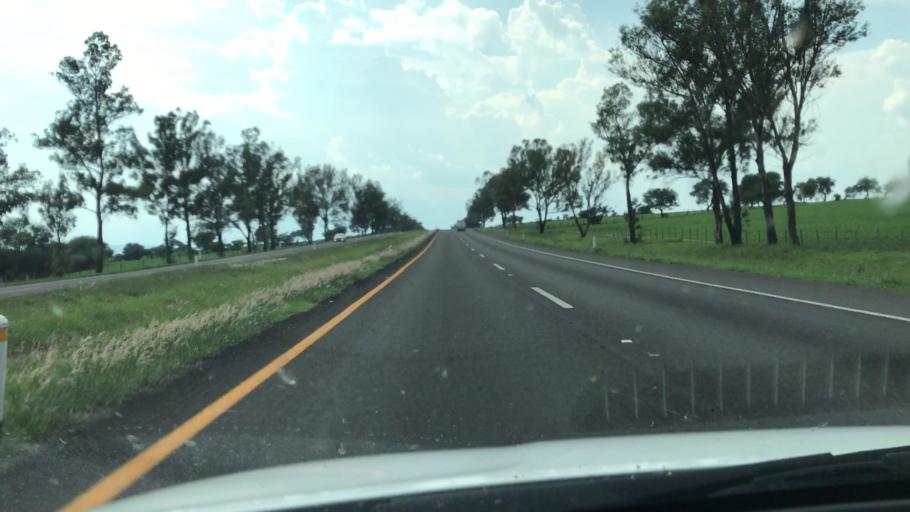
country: MX
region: Jalisco
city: Jamay
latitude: 20.3607
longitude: -102.6448
